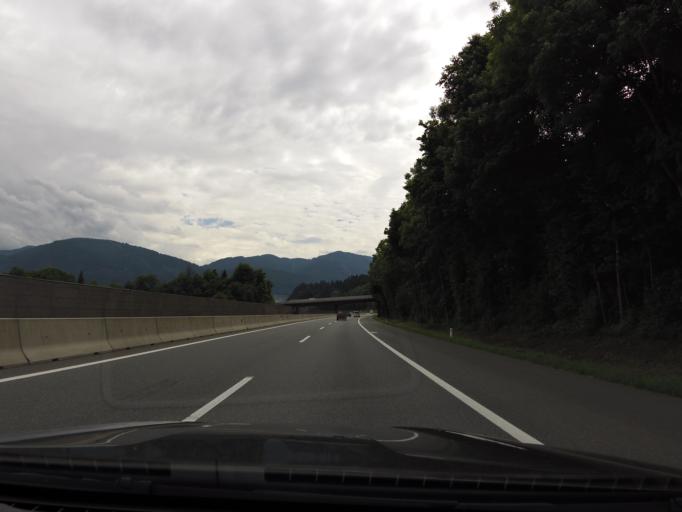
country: AT
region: Tyrol
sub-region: Politischer Bezirk Kufstein
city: Angath
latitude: 47.5100
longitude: 12.0631
